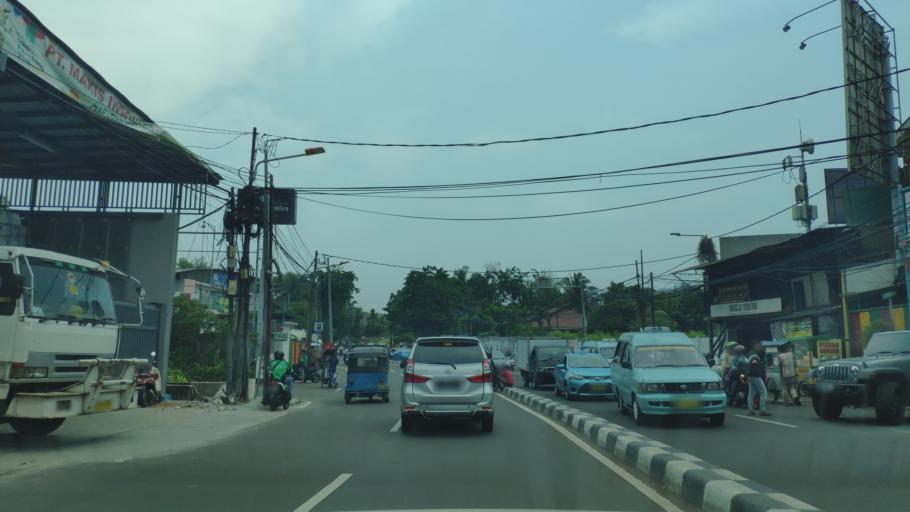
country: ID
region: Jakarta Raya
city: Jakarta
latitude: -6.1992
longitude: 106.8025
